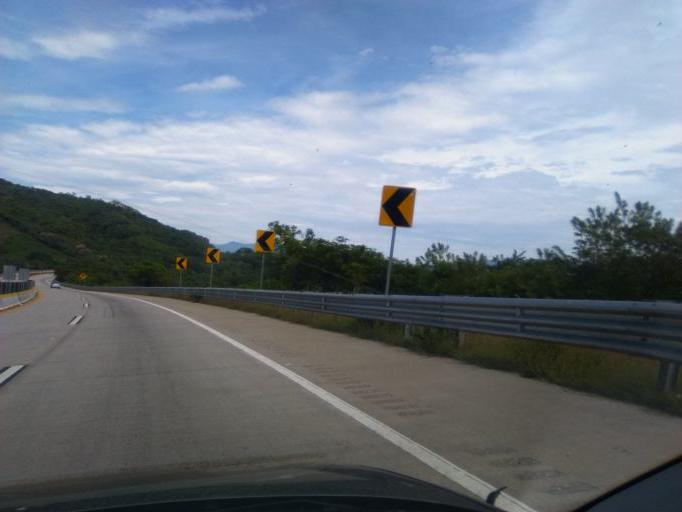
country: MX
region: Guerrero
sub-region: Acapulco de Juarez
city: Pueblo Madero (El Playon)
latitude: 17.0296
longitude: -99.6408
